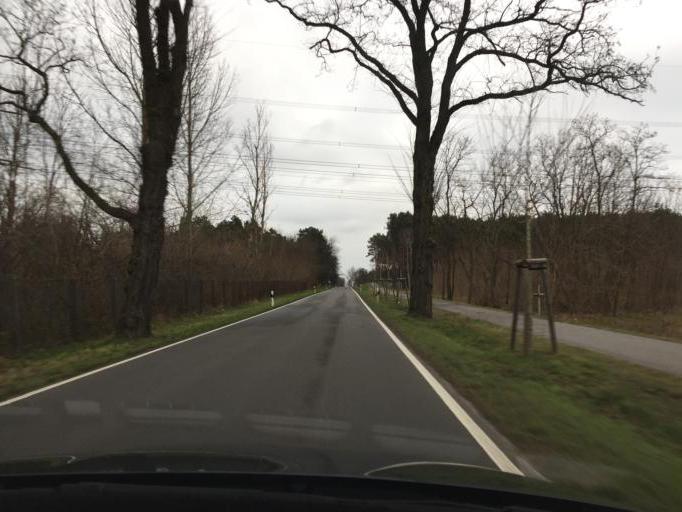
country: DE
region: Brandenburg
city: Gross Lindow
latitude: 52.1199
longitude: 14.5097
